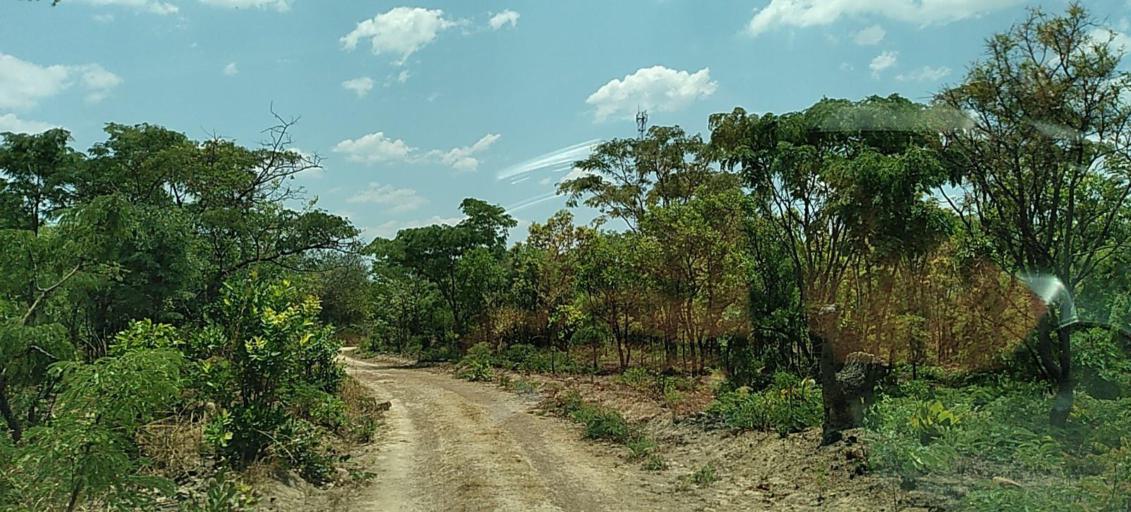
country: ZM
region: Copperbelt
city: Chililabombwe
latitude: -12.4502
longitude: 27.6791
